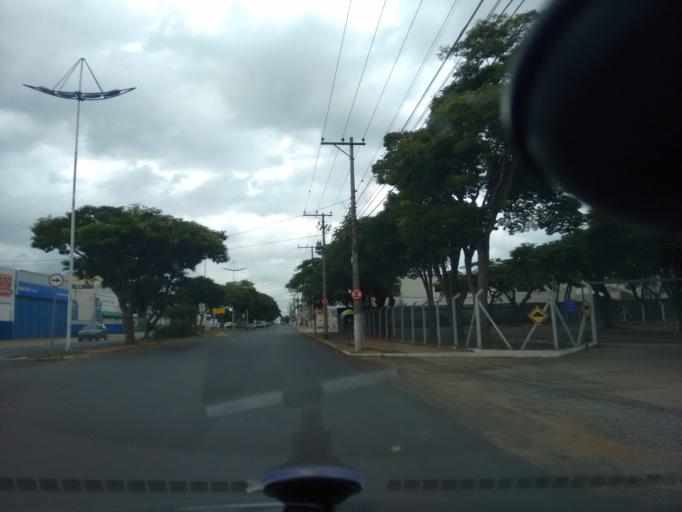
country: BR
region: Sao Paulo
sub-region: Indaiatuba
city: Indaiatuba
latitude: -23.0860
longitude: -47.1977
